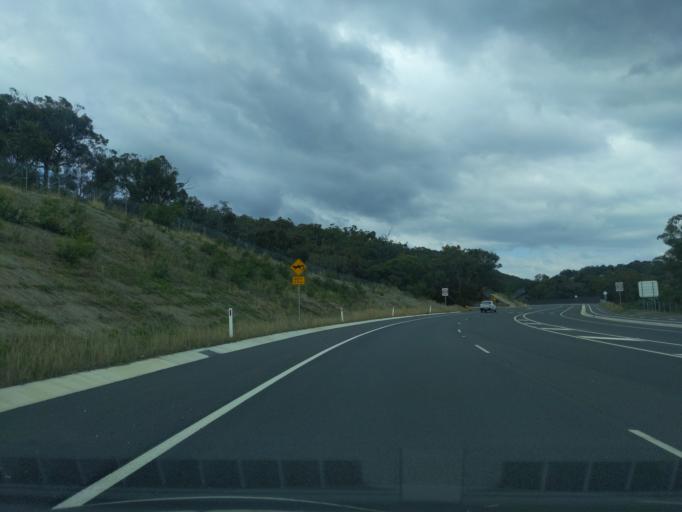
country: AU
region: New South Wales
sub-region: Queanbeyan
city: Queanbeyan
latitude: -35.3537
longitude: 149.2532
